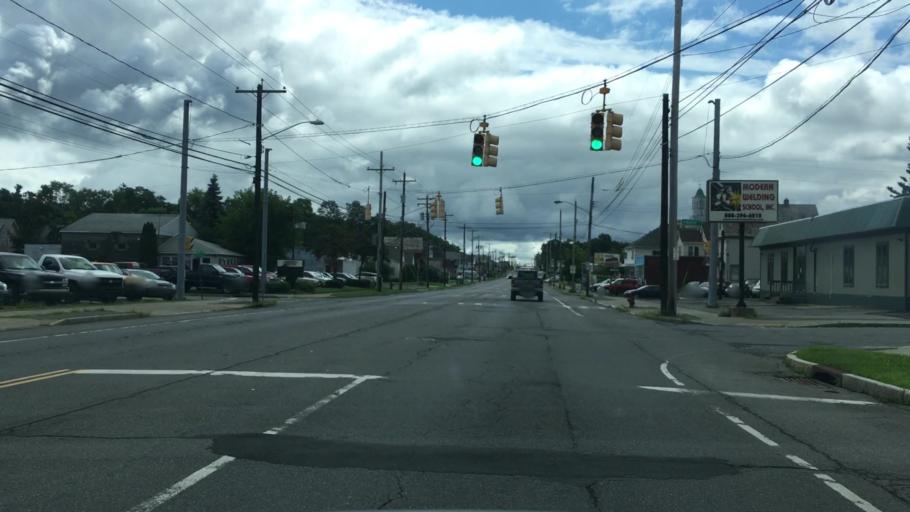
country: US
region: New York
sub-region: Schenectady County
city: Schenectady
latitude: 42.7796
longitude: -73.9032
